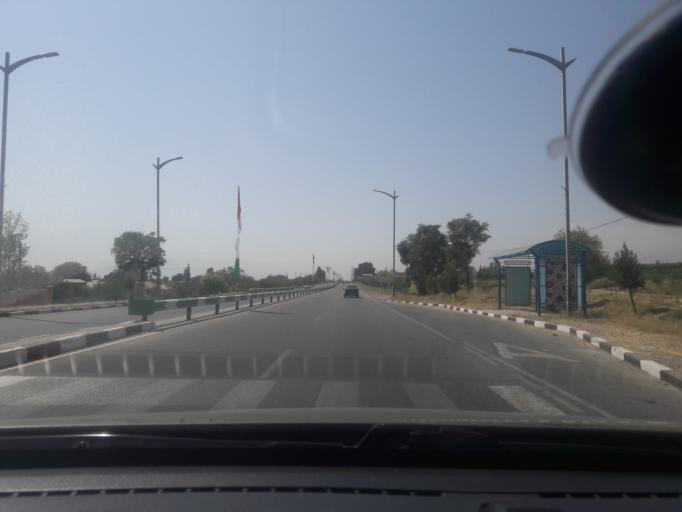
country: TJ
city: Shahrinav
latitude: 38.5612
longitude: 68.4442
